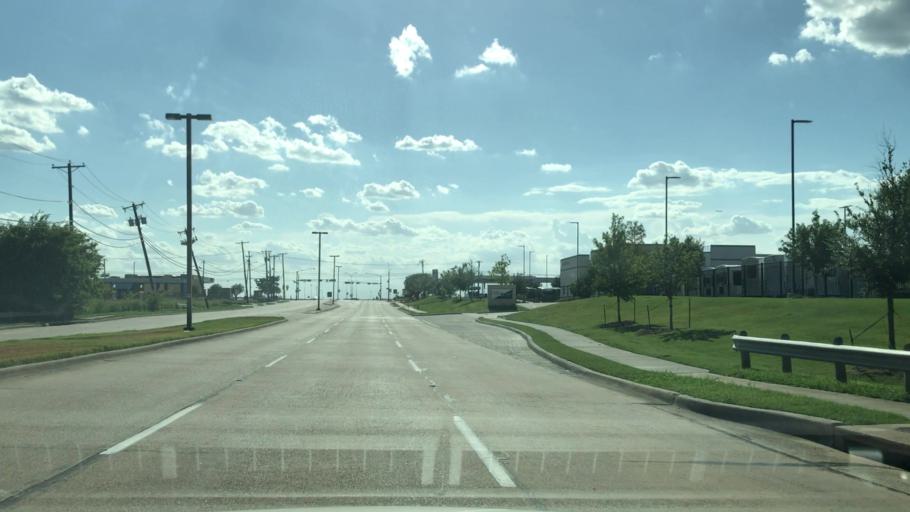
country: US
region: Texas
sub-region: Tarrant County
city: Euless
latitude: 32.8571
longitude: -97.0183
